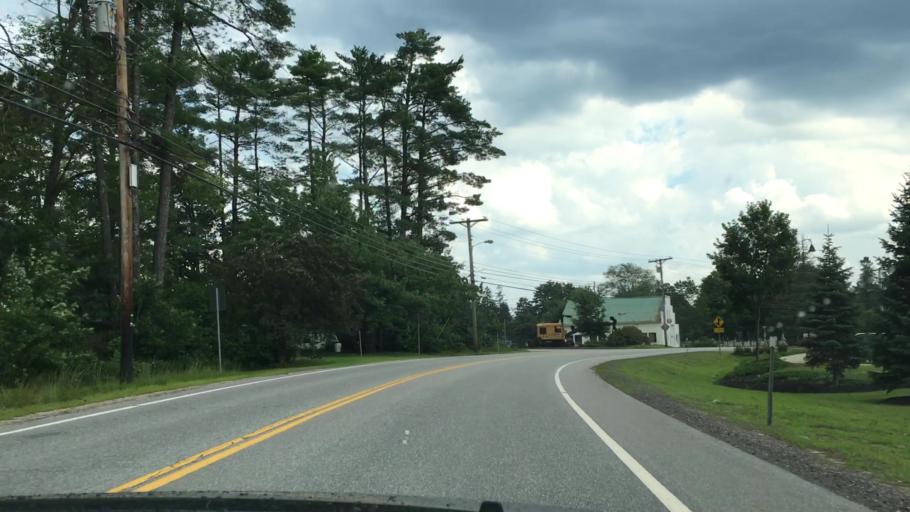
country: US
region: New Hampshire
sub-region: Belknap County
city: Meredith
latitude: 43.6710
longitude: -71.5031
